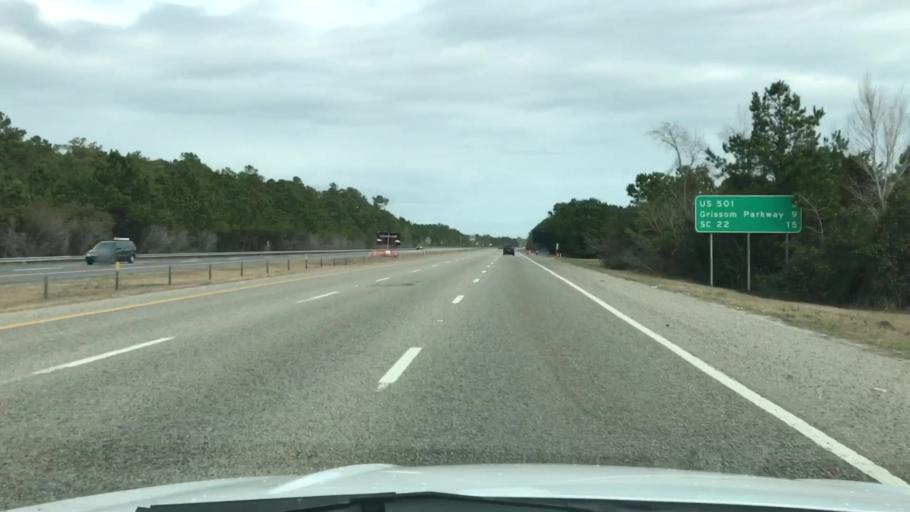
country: US
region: South Carolina
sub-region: Horry County
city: Socastee
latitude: 33.7162
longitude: -79.0018
